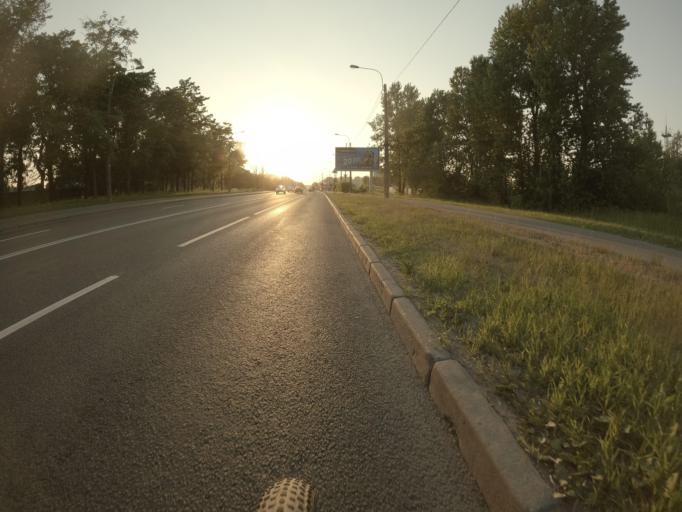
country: RU
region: St.-Petersburg
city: Avtovo
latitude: 59.8645
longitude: 30.2816
